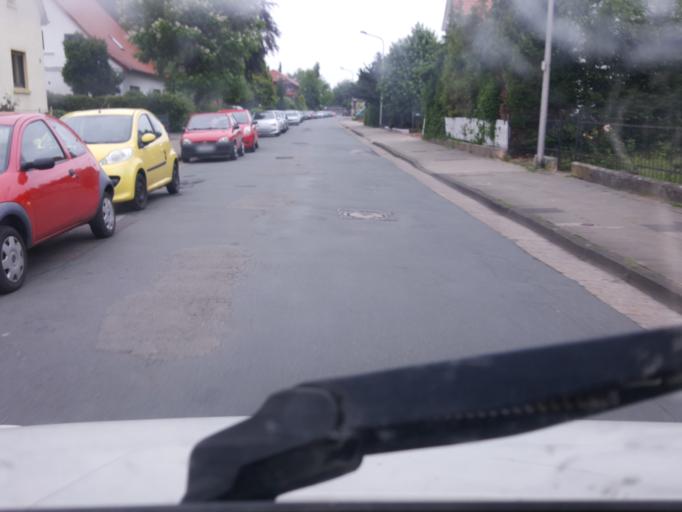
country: DE
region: North Rhine-Westphalia
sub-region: Regierungsbezirk Detmold
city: Minden
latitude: 52.2983
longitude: 8.8966
